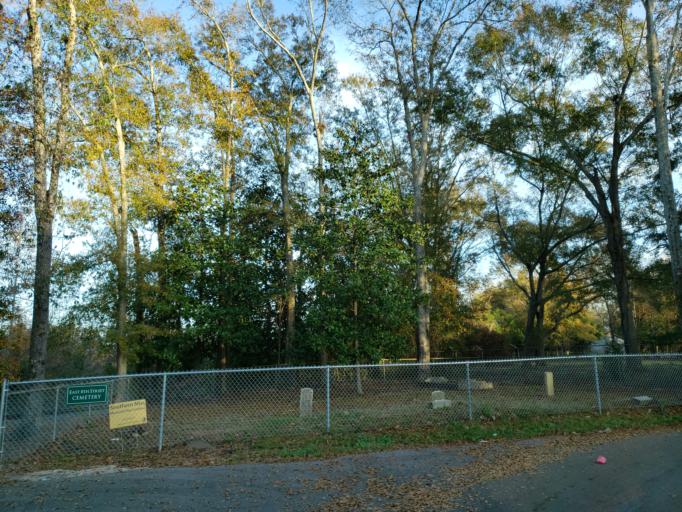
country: US
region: Mississippi
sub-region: Forrest County
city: Hattiesburg
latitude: 31.3372
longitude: -89.2972
